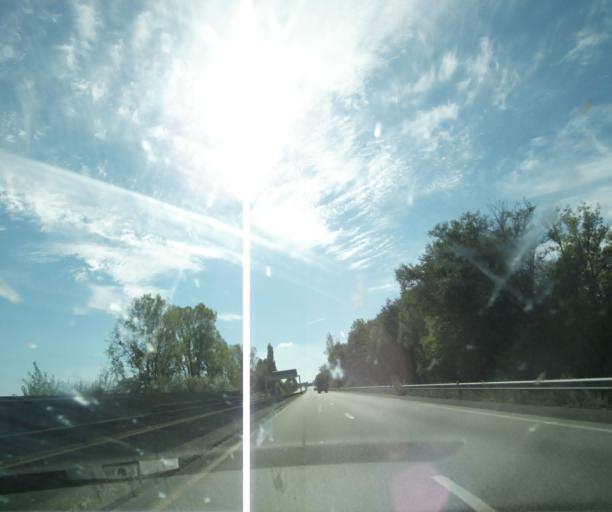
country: FR
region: Limousin
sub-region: Departement de la Correze
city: Ussac
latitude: 45.1718
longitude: 1.4860
